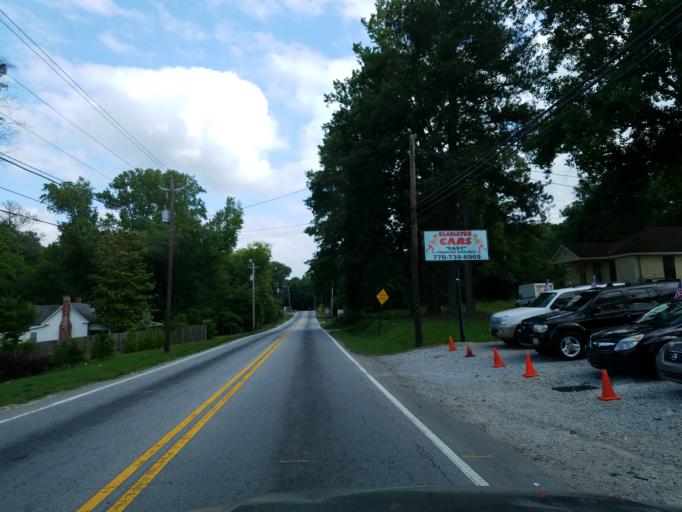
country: US
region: Georgia
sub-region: Douglas County
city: Lithia Springs
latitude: 33.7930
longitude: -84.6604
